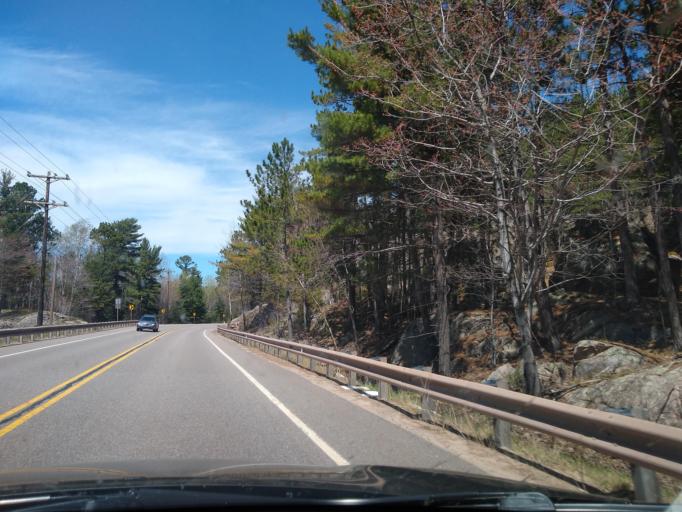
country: US
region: Michigan
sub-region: Marquette County
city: Trowbridge Park
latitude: 46.6100
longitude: -87.4698
